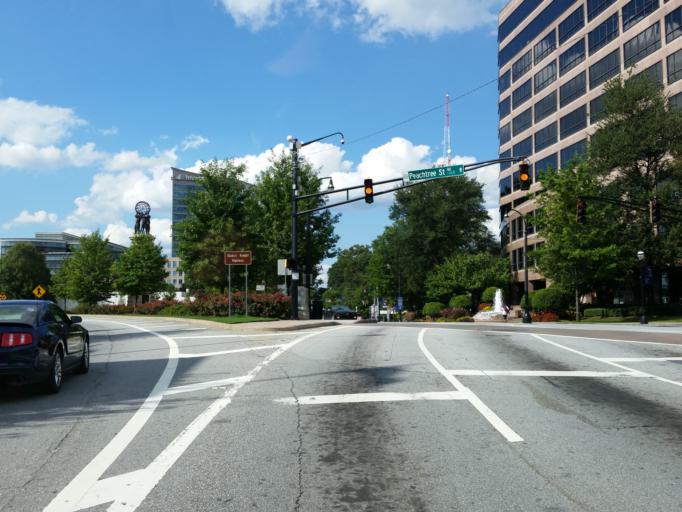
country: US
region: Georgia
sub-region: Fulton County
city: Atlanta
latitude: 33.7942
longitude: -84.3878
